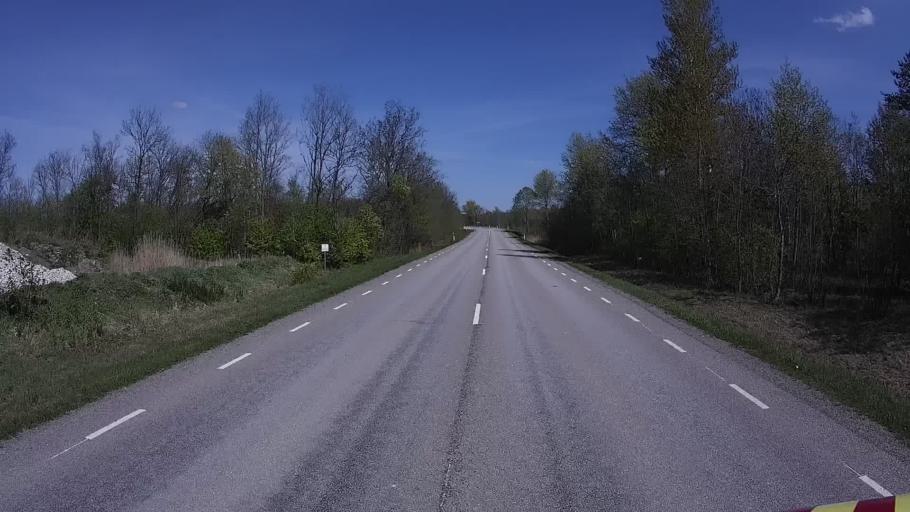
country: EE
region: Laeaene
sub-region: Ridala Parish
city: Uuemoisa
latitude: 58.9642
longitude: 23.6735
